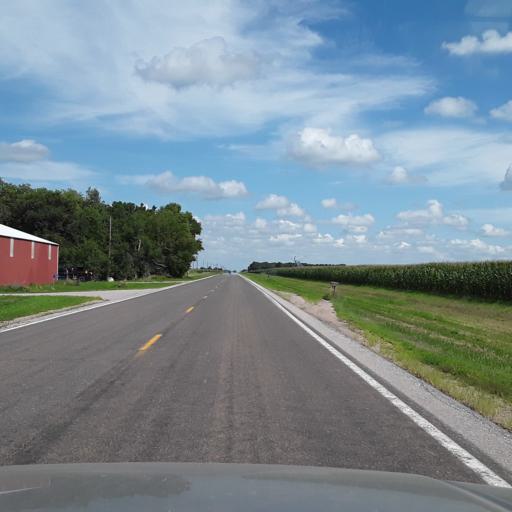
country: US
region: Nebraska
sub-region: Polk County
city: Osceola
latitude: 41.0390
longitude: -97.4063
